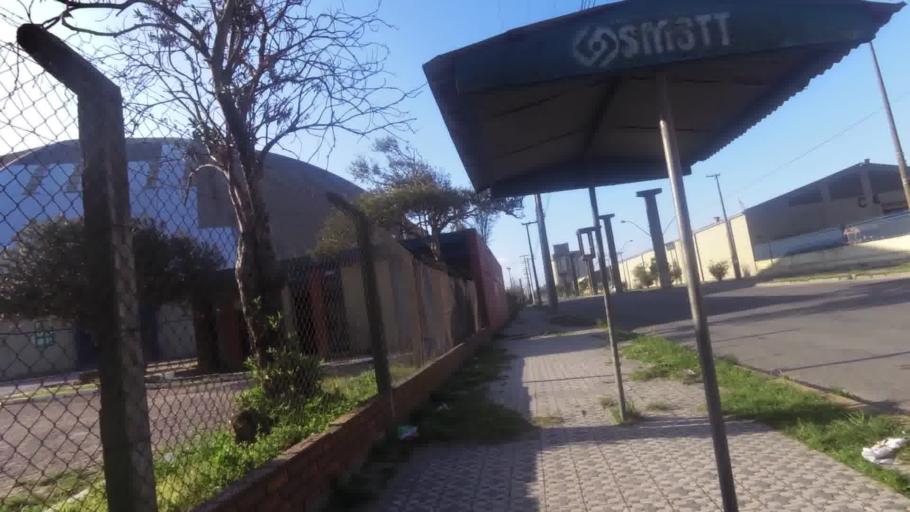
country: BR
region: Rio Grande do Sul
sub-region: Rio Grande
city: Rio Grande
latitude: -32.0401
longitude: -52.0775
